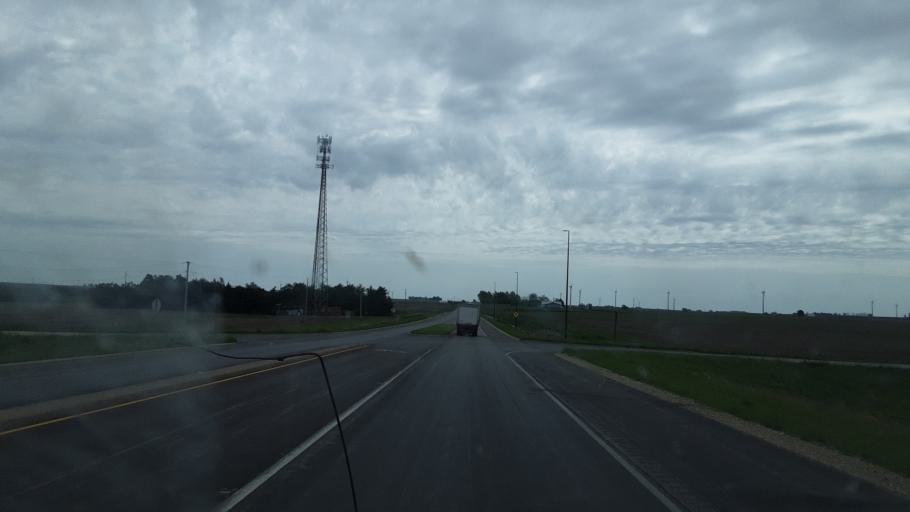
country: US
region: Illinois
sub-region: Tazewell County
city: Richmond
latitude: 40.3082
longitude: -89.4500
